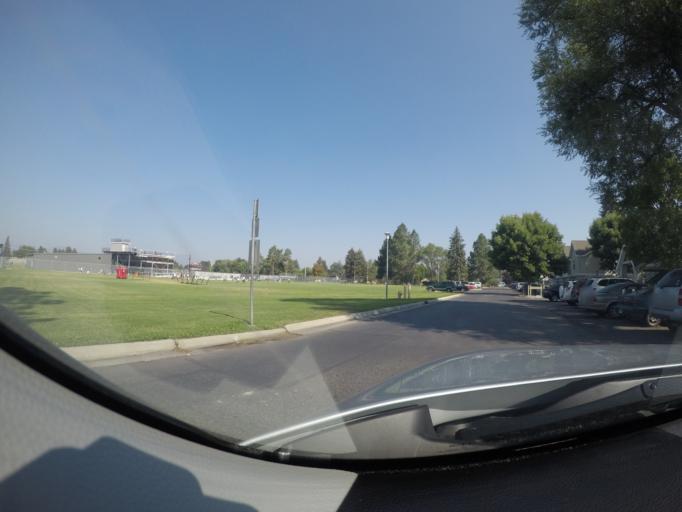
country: US
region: Montana
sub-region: Missoula County
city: Missoula
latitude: 46.8474
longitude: -113.9933
